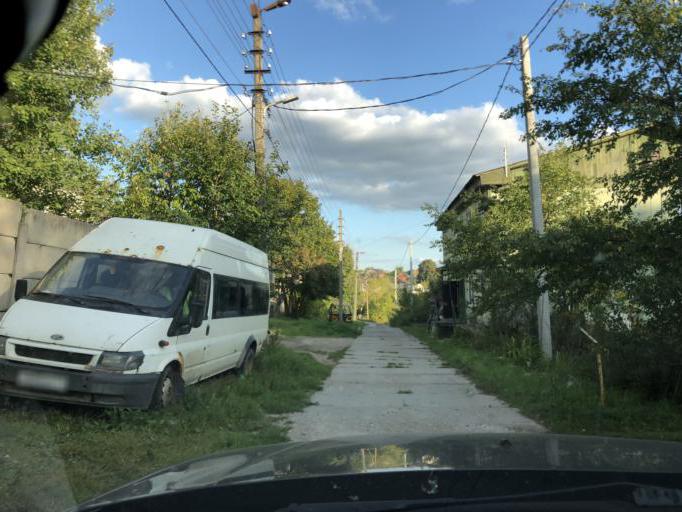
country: RU
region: Tula
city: Mendeleyevskiy
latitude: 54.1831
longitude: 37.5434
